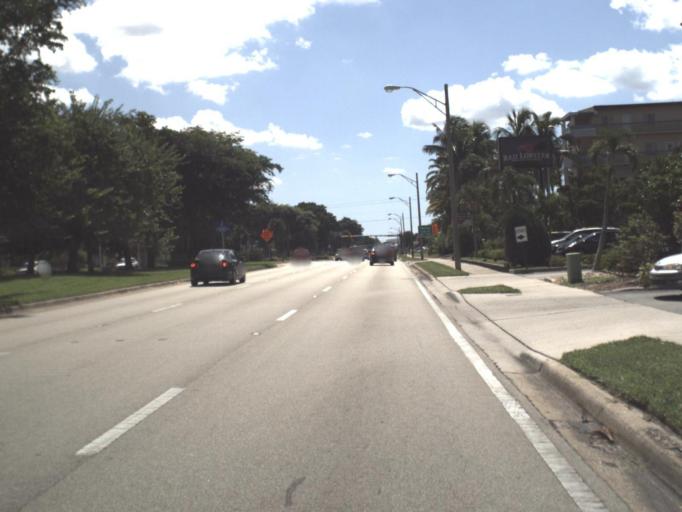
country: US
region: Florida
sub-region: Collier County
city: Naples
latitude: 26.1772
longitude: -81.7999
